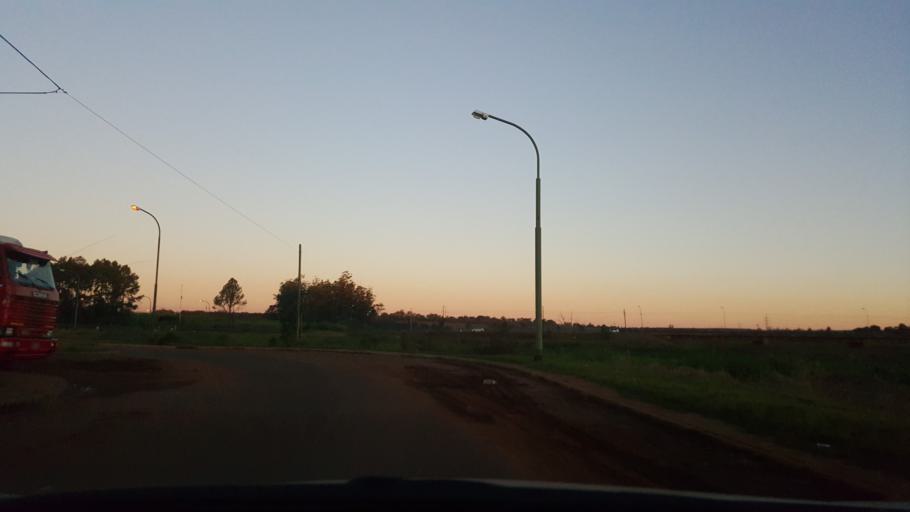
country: AR
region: Misiones
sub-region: Departamento de Capital
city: Posadas
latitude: -27.4263
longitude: -55.9028
